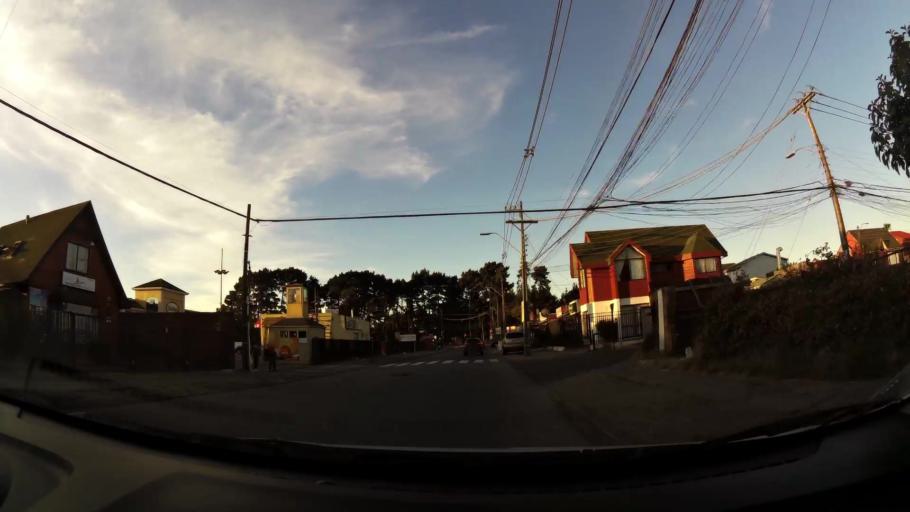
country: CL
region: Biobio
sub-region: Provincia de Concepcion
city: Concepcion
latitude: -36.8401
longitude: -73.0955
